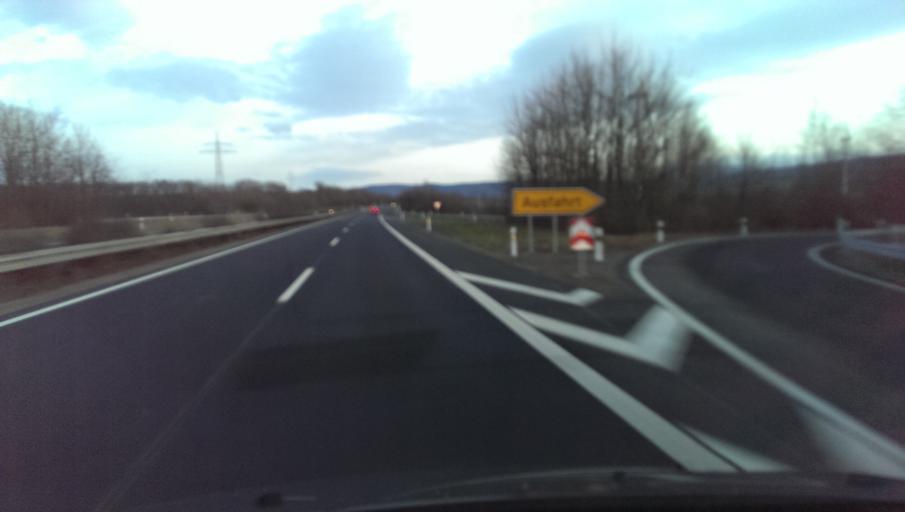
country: DE
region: Lower Saxony
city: Vienenburg
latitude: 51.9257
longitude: 10.5067
